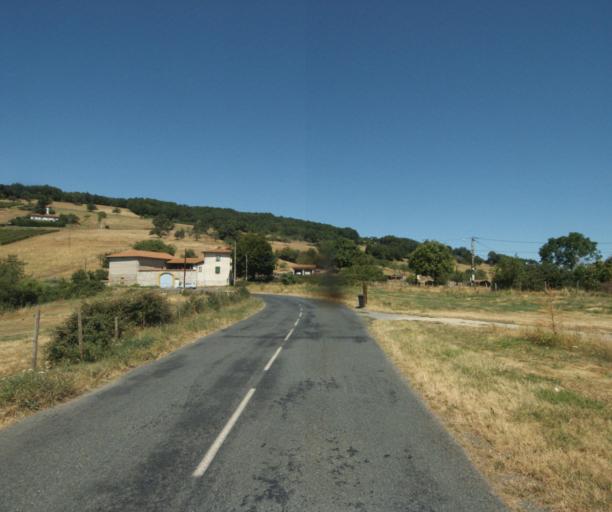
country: FR
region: Rhone-Alpes
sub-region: Departement du Rhone
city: Bessenay
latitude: 45.7933
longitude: 4.5424
